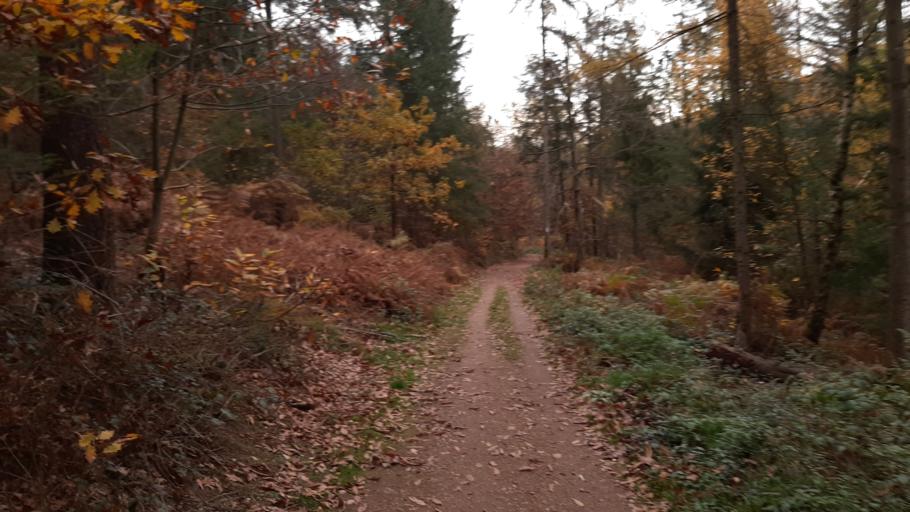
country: DE
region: Saarland
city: Mettlach
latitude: 49.4937
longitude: 6.5755
